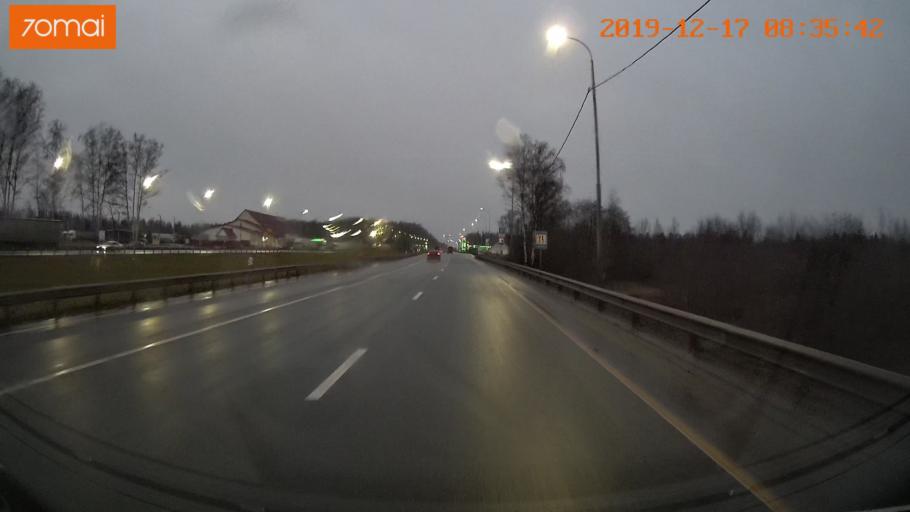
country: RU
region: Vladimir
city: Lakinsk
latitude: 55.9975
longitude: 39.8975
